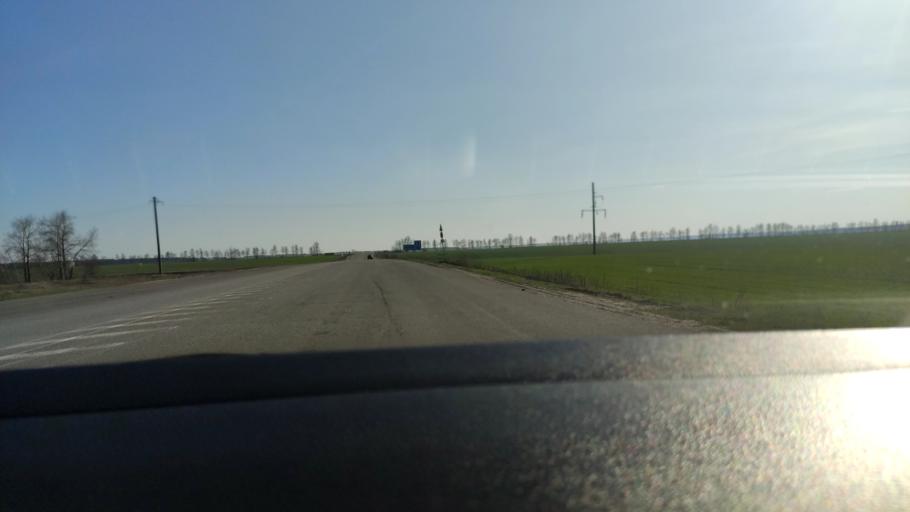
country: RU
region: Voronezj
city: Kolodeznyy
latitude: 51.3991
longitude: 39.2369
